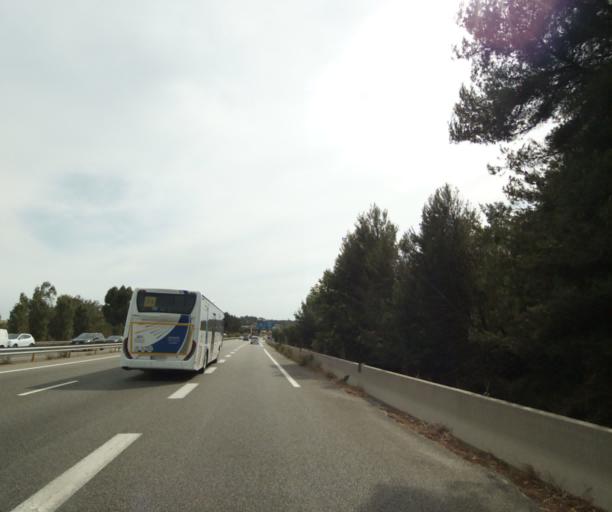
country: FR
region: Provence-Alpes-Cote d'Azur
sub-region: Departement du Var
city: La Farlede
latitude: 43.1473
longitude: 6.0327
